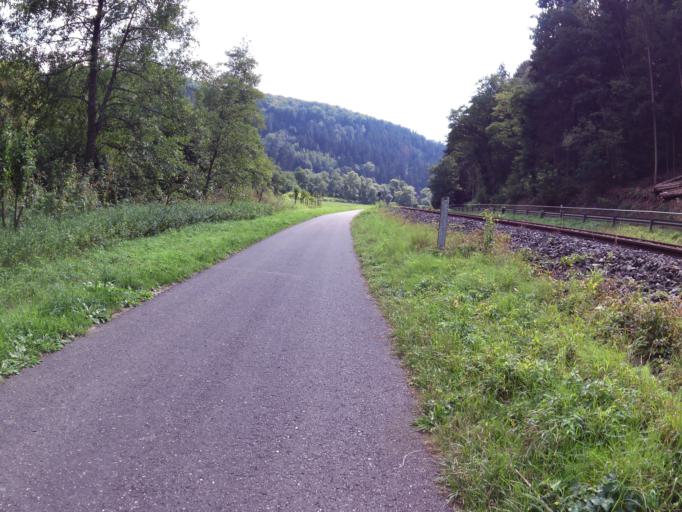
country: DE
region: Rheinland-Pfalz
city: Kordel
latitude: 49.8317
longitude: 6.6496
